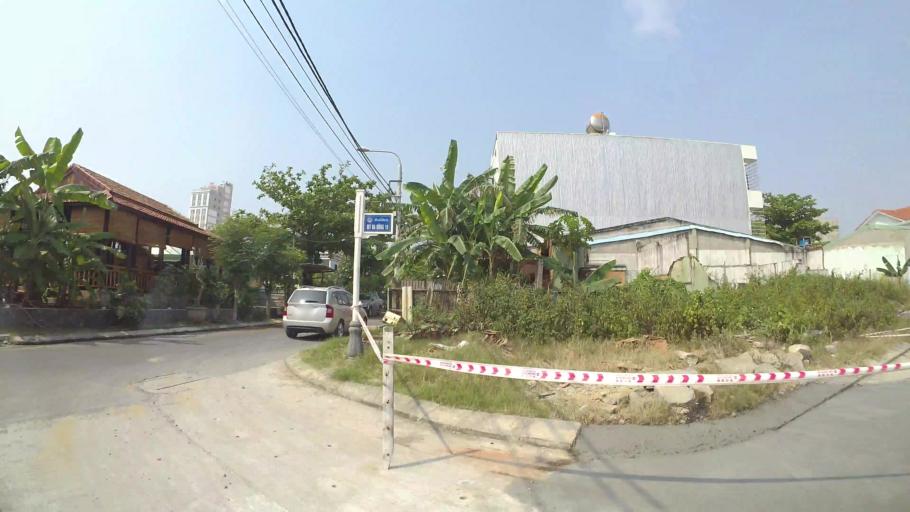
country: VN
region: Da Nang
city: Son Tra
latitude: 16.0455
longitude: 108.2484
